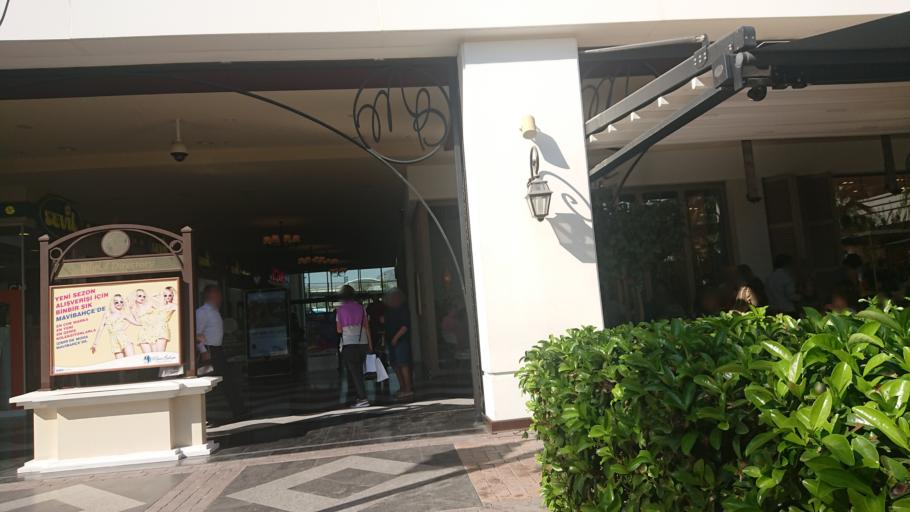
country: TR
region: Izmir
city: Karsiyaka
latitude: 38.4744
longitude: 27.0748
